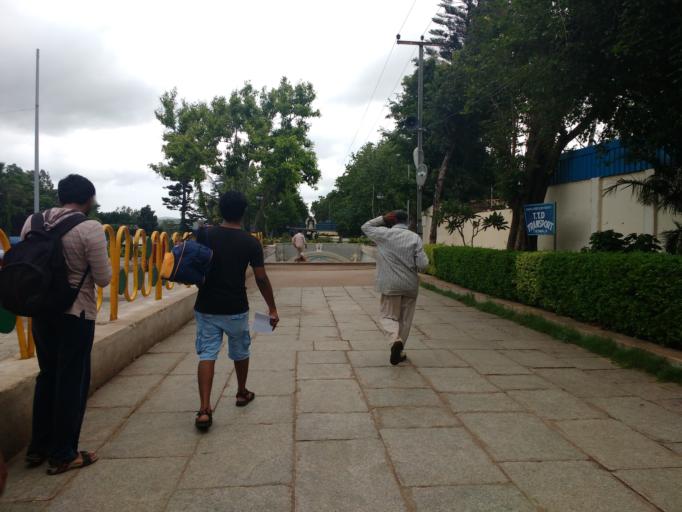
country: IN
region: Andhra Pradesh
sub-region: Chittoor
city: Tirumala
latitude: 13.6733
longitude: 79.3515
